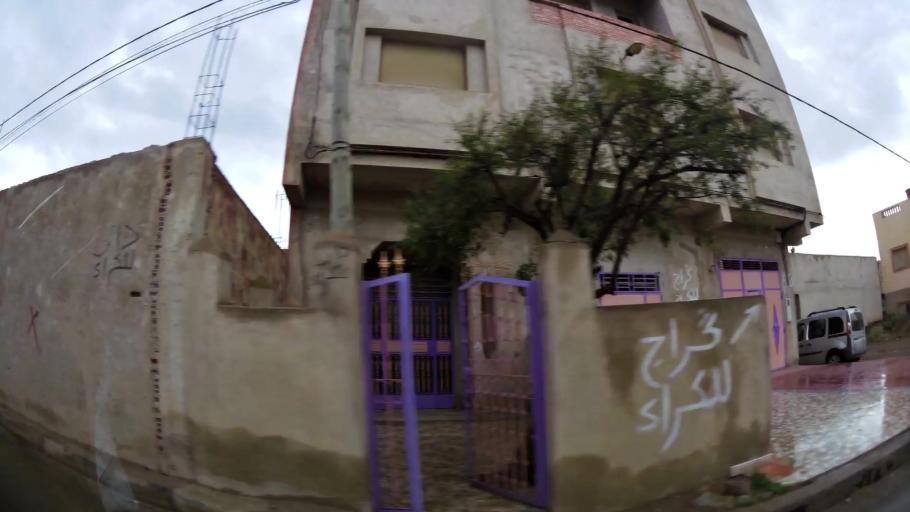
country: MA
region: Oriental
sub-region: Nador
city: Nador
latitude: 35.1489
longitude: -2.9862
